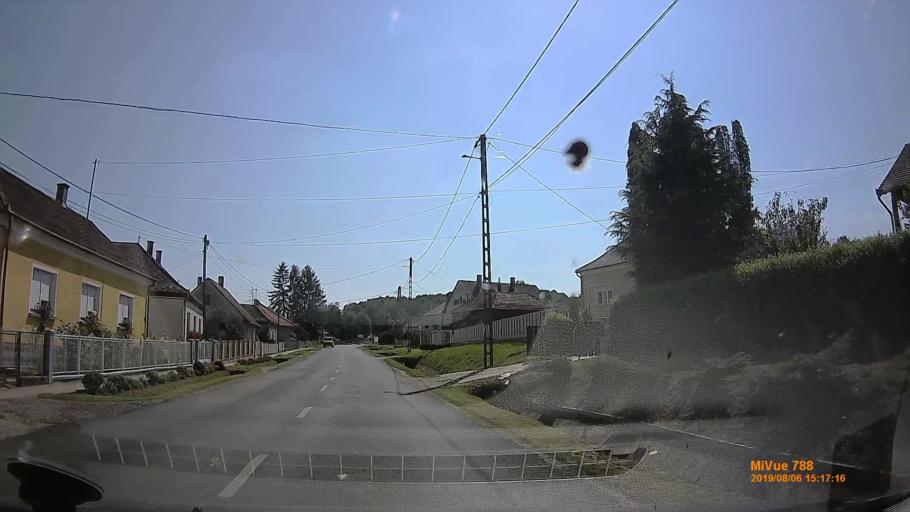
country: HU
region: Zala
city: Murakeresztur
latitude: 46.3164
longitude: 16.9655
